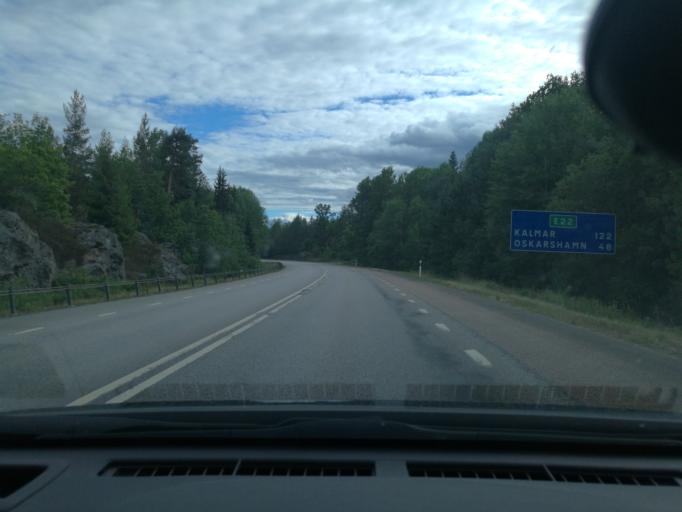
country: SE
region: Kalmar
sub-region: Vasterviks Kommun
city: Ankarsrum
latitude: 57.6548
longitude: 16.4422
